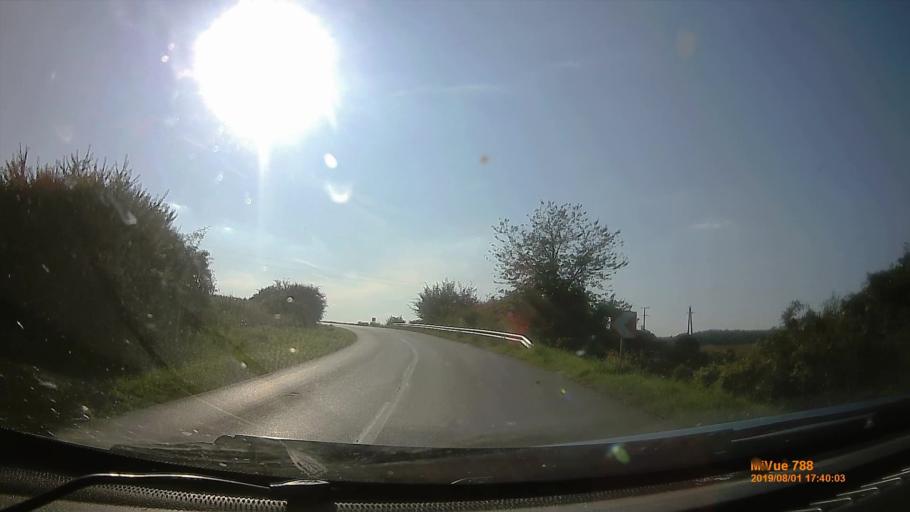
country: HU
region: Baranya
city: Komlo
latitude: 46.2014
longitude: 18.1874
